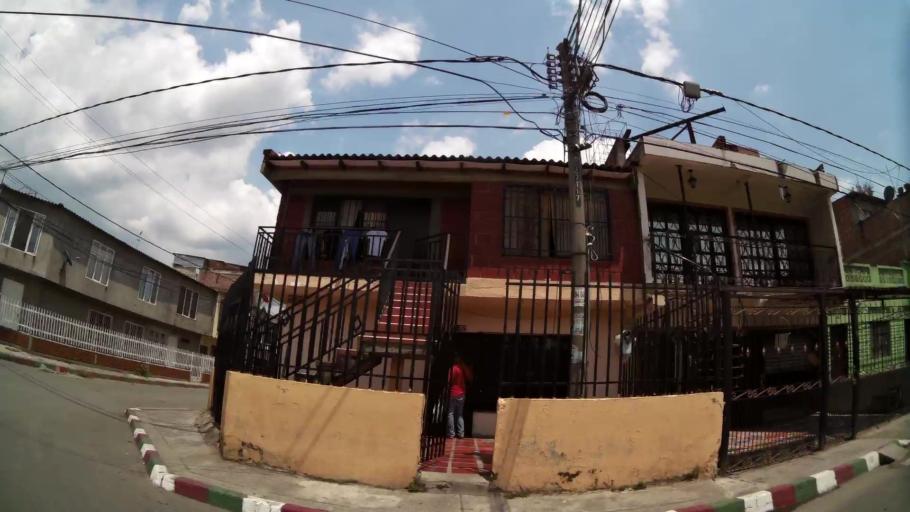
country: CO
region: Valle del Cauca
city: Cali
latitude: 3.4488
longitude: -76.4808
